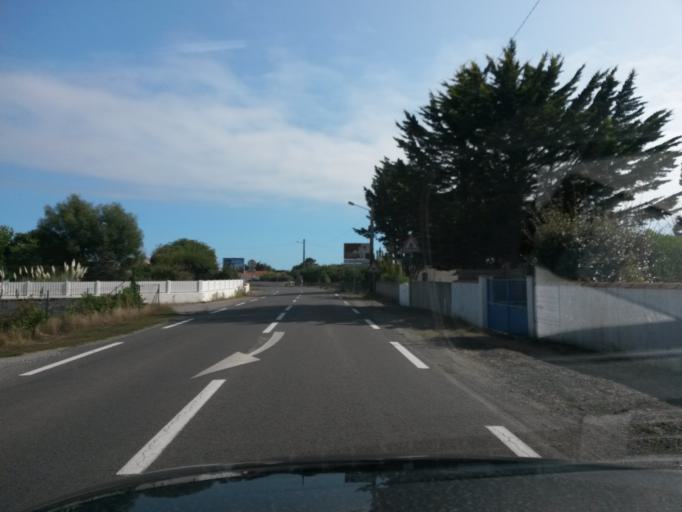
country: FR
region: Pays de la Loire
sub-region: Departement de la Vendee
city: Olonne-sur-Mer
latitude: 46.5553
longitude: -1.8107
